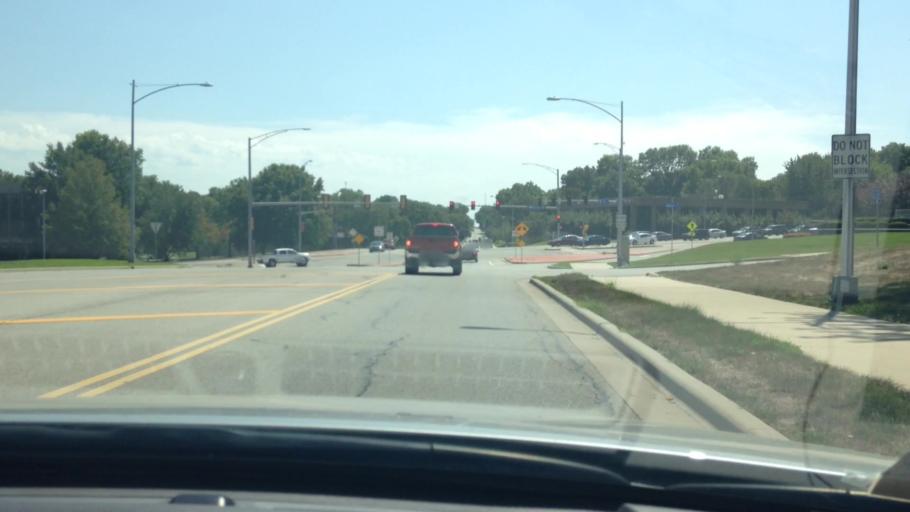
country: US
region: Kansas
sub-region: Johnson County
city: Mission
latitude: 39.0170
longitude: -94.6491
